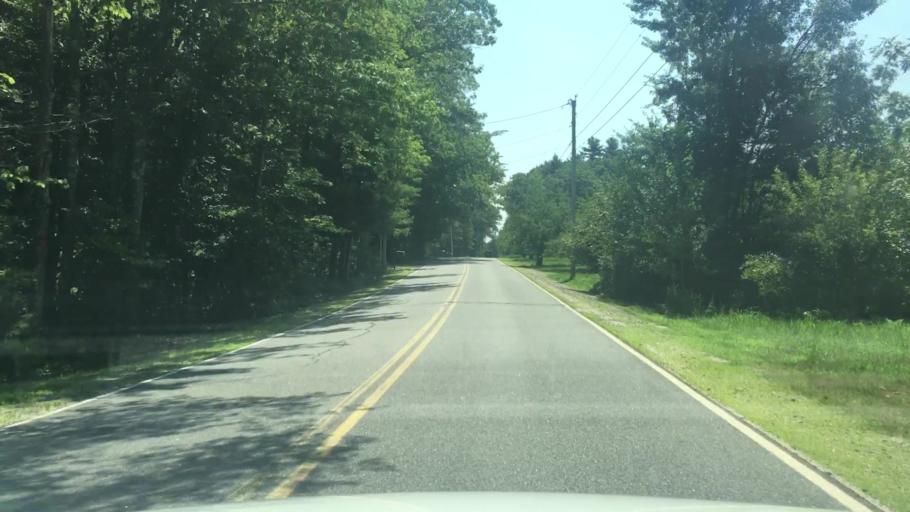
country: US
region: Maine
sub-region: Cumberland County
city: Cumberland Center
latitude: 43.8353
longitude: -70.3040
